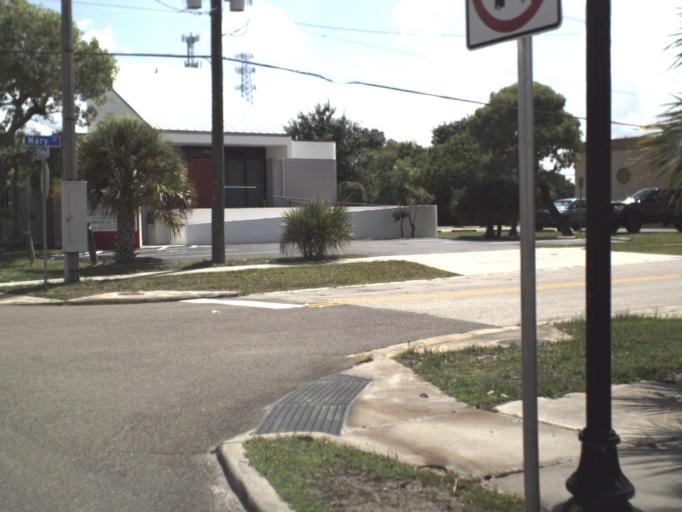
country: US
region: Florida
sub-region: Charlotte County
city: Punta Gorda
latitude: 26.9386
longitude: -82.0426
